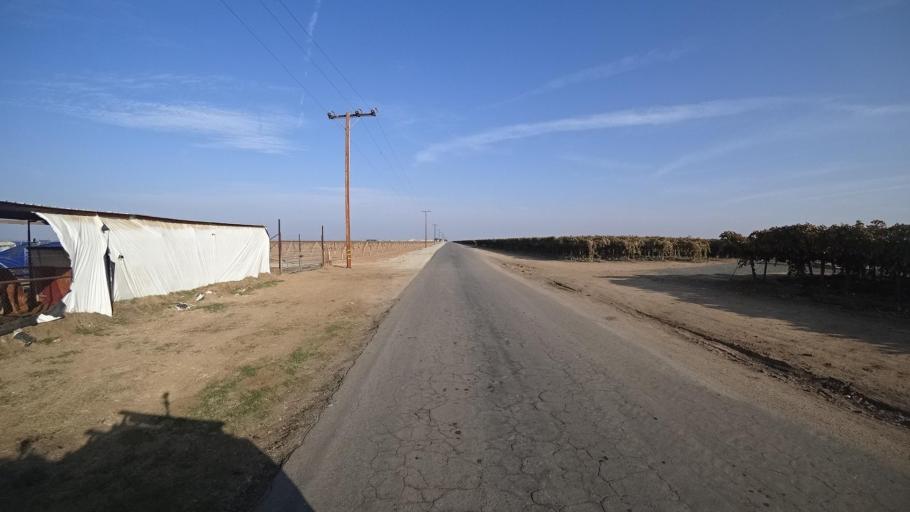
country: US
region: California
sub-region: Kern County
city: McFarland
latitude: 35.6895
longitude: -119.1870
